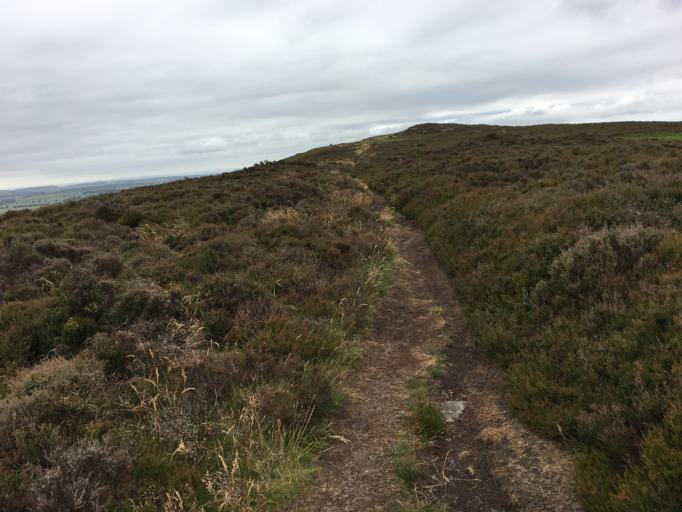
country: GB
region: England
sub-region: Northumberland
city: Lowick
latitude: 55.6130
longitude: -1.9086
